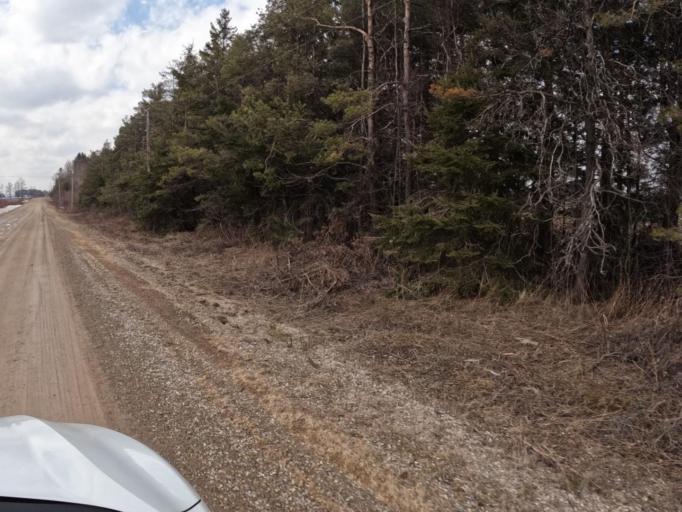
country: CA
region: Ontario
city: Shelburne
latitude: 44.0269
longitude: -80.2653
